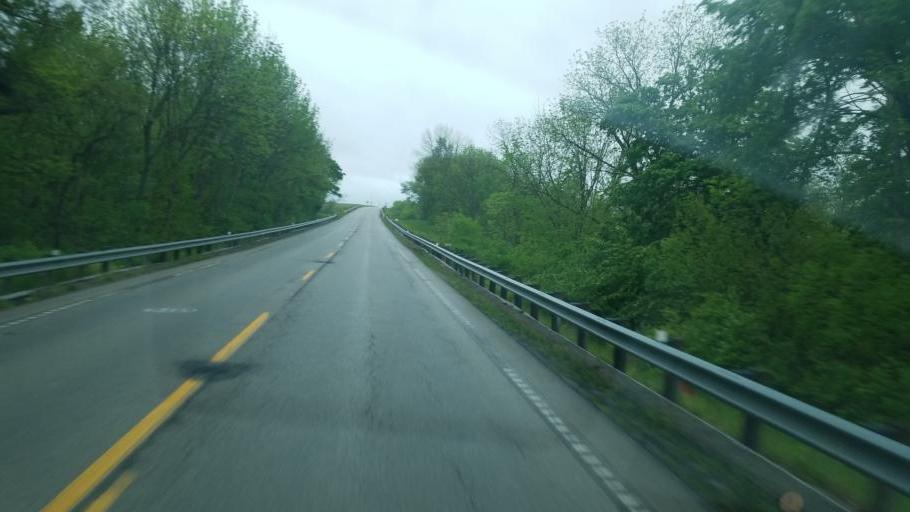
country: US
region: Ohio
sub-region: Highland County
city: Leesburg
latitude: 39.3016
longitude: -83.5813
